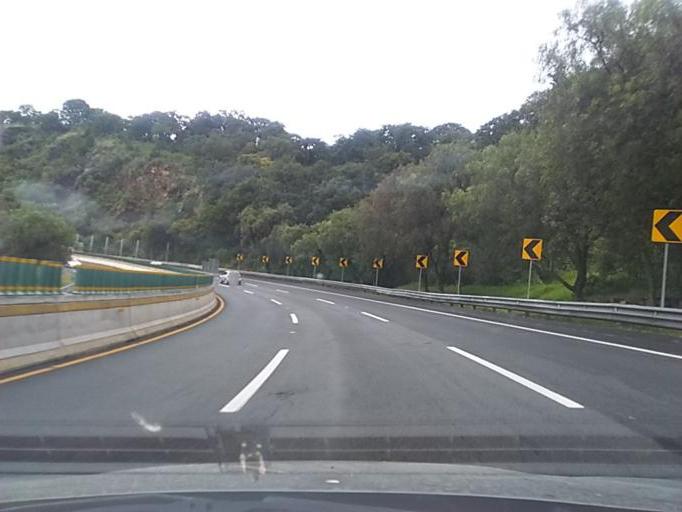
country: MX
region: Mexico City
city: Xochimilco
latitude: 19.2229
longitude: -99.1372
